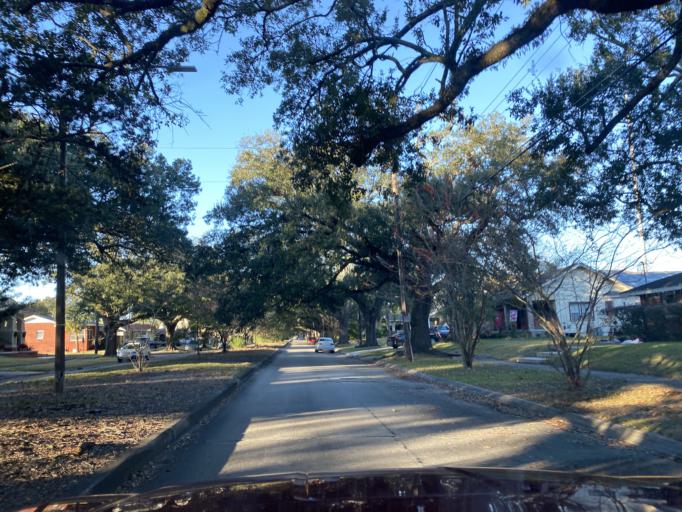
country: US
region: Louisiana
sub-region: Orleans Parish
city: New Orleans
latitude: 30.0042
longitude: -90.0550
